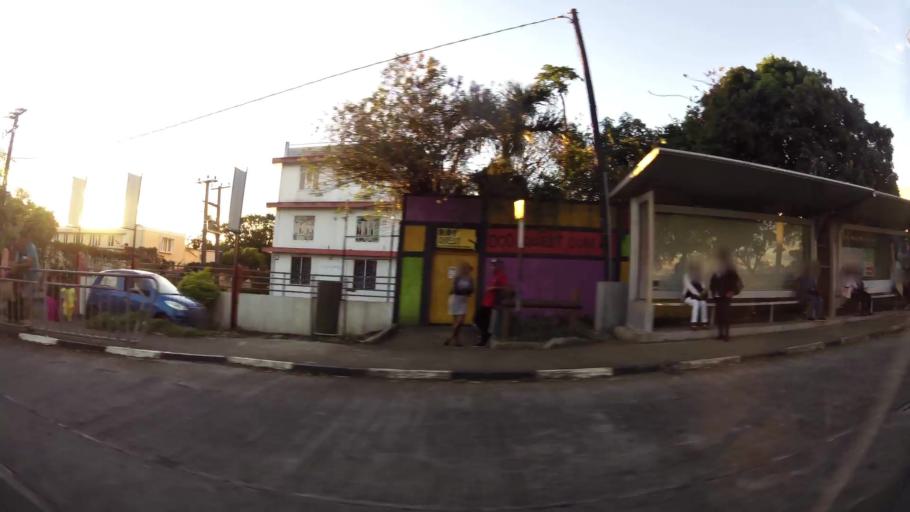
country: MU
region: Moka
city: Moka
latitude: -20.2263
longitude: 57.5064
